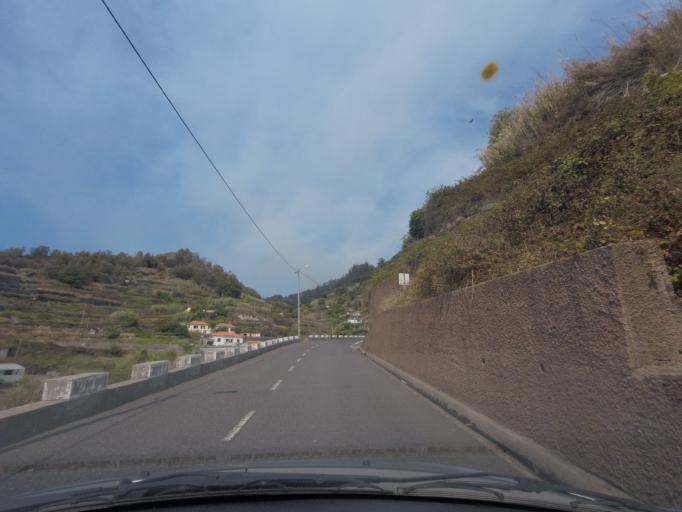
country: PT
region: Madeira
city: Ponta do Sol
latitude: 32.6883
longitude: -17.0692
